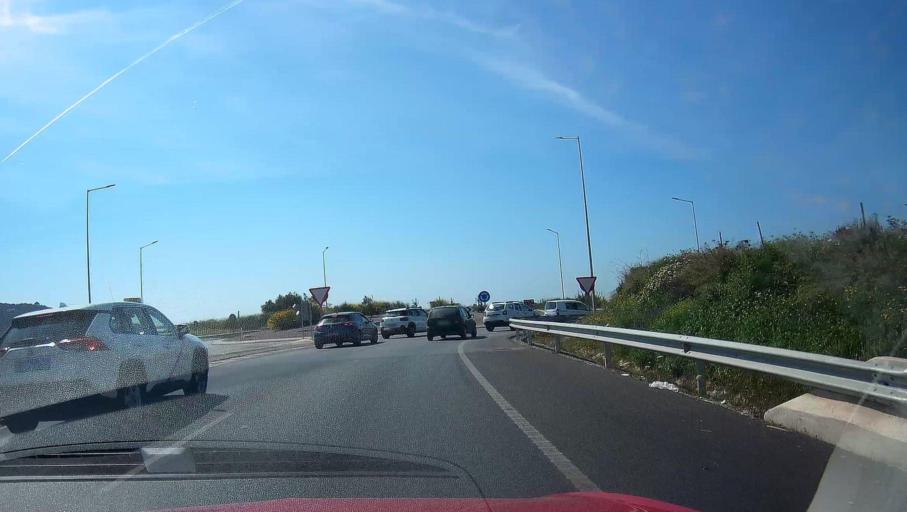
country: ES
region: Balearic Islands
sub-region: Illes Balears
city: Ibiza
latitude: 38.9429
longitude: 1.4439
